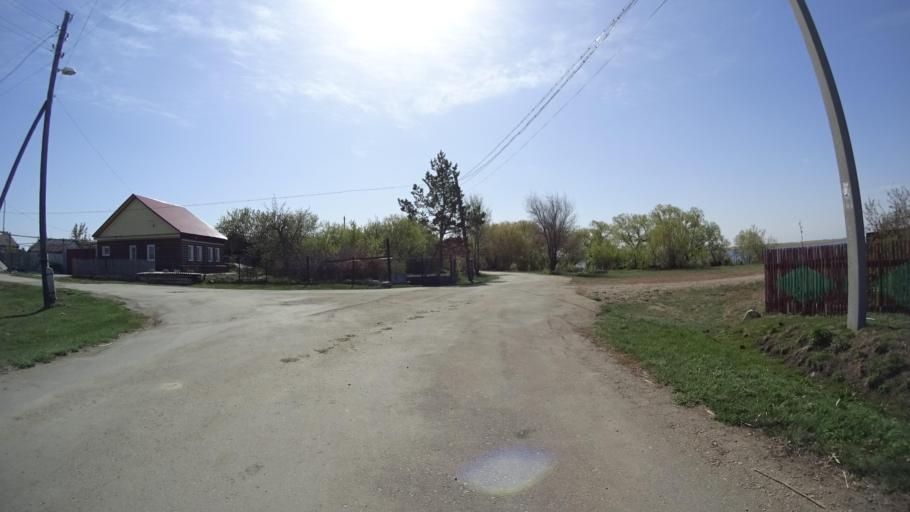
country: RU
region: Chelyabinsk
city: Chesma
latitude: 53.7975
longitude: 61.0236
